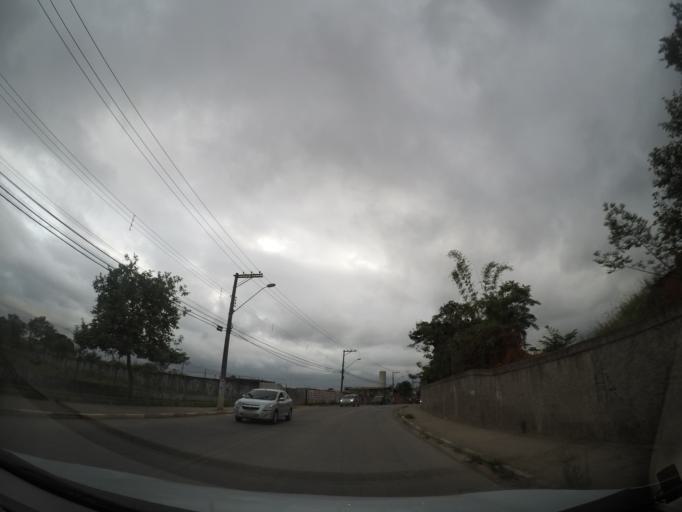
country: BR
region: Sao Paulo
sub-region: Guarulhos
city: Guarulhos
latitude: -23.4064
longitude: -46.4384
